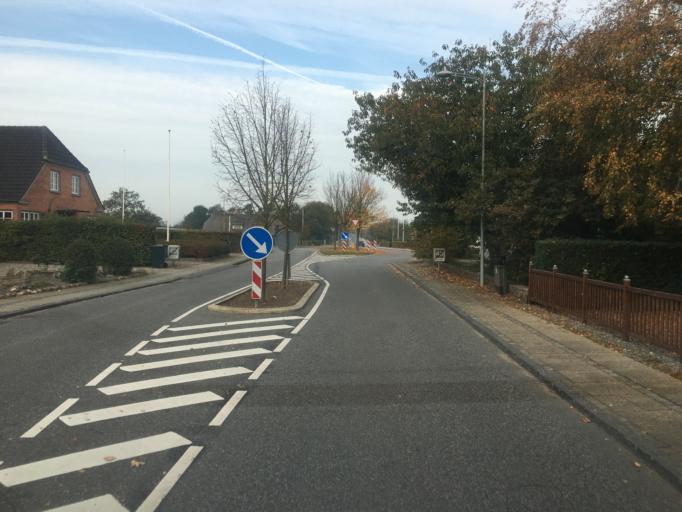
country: DK
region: South Denmark
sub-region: Tonder Kommune
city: Toftlund
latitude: 55.1209
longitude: 9.0676
